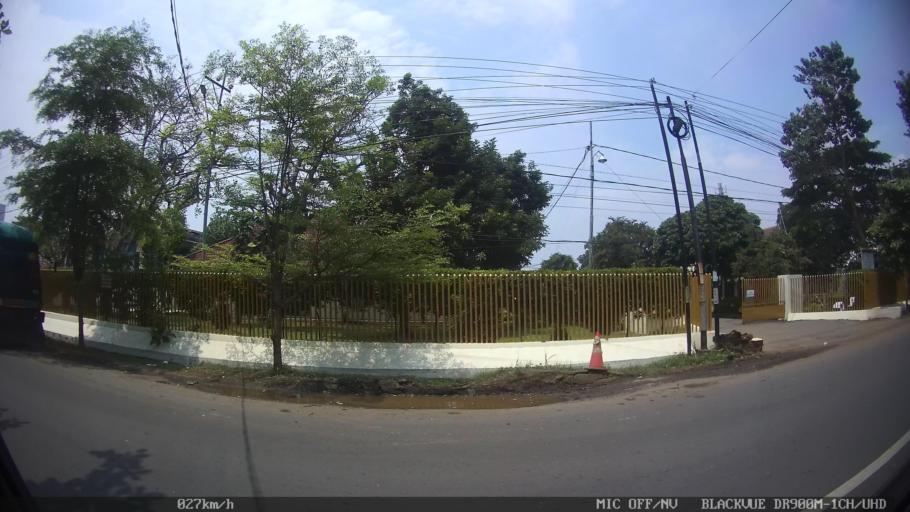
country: ID
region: Lampung
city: Bandarlampung
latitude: -5.4360
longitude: 105.2846
